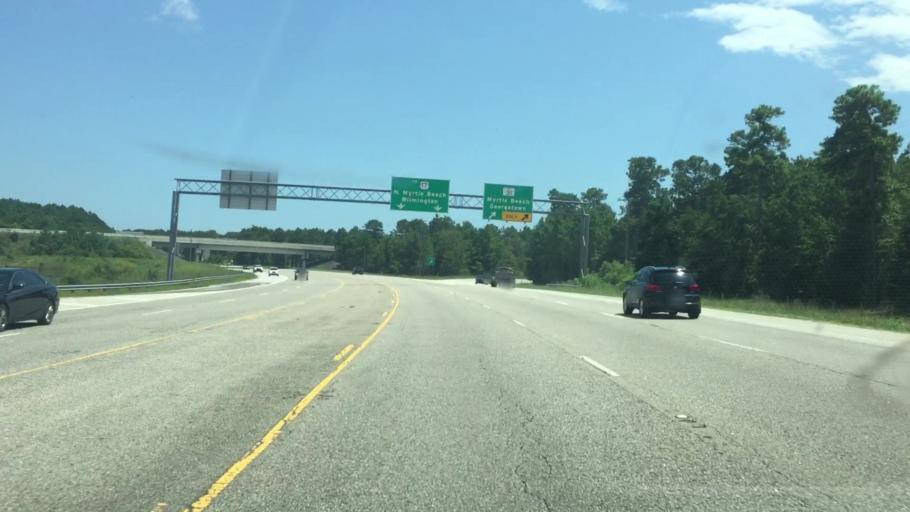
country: US
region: South Carolina
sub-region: Horry County
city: North Myrtle Beach
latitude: 33.8776
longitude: -78.6849
